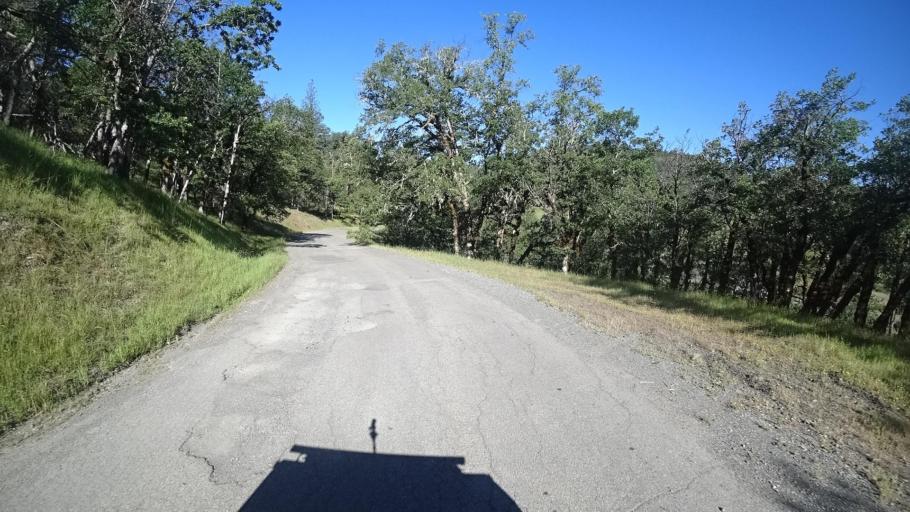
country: US
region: California
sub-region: Lake County
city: Upper Lake
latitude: 39.4087
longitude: -122.9777
